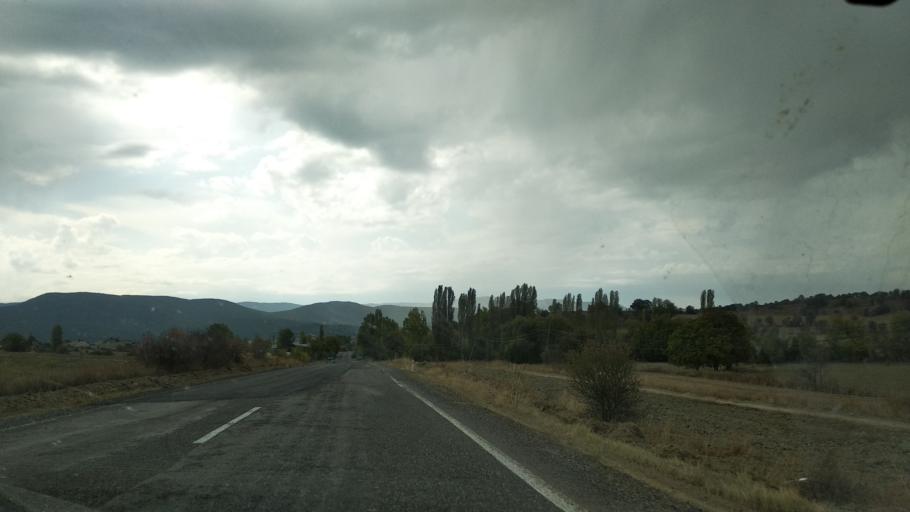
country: TR
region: Bolu
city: Seben
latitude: 40.3454
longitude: 31.4740
